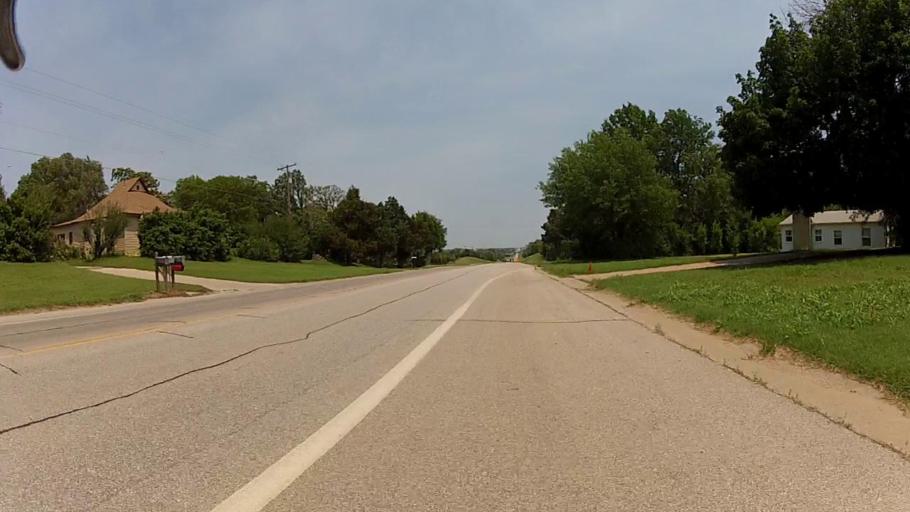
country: US
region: Kansas
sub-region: Cowley County
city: Arkansas City
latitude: 37.0565
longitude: -97.0775
